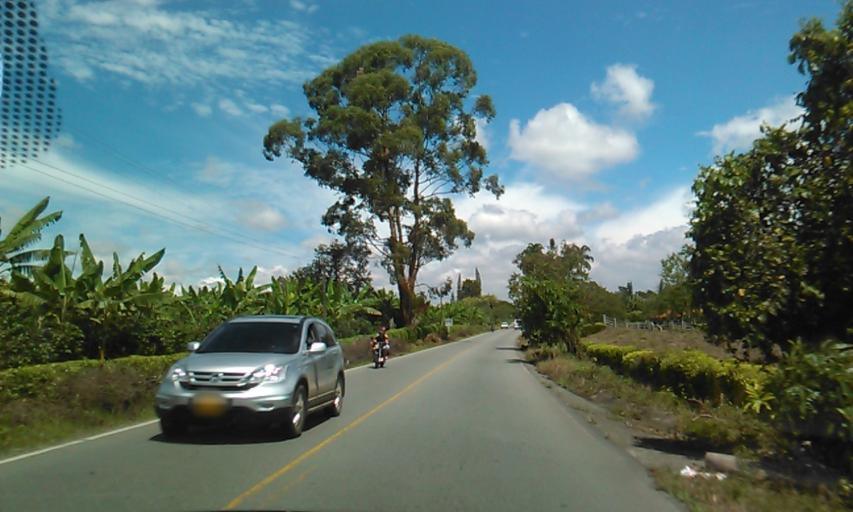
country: CO
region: Quindio
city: Cordoba
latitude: 4.4472
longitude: -75.7171
